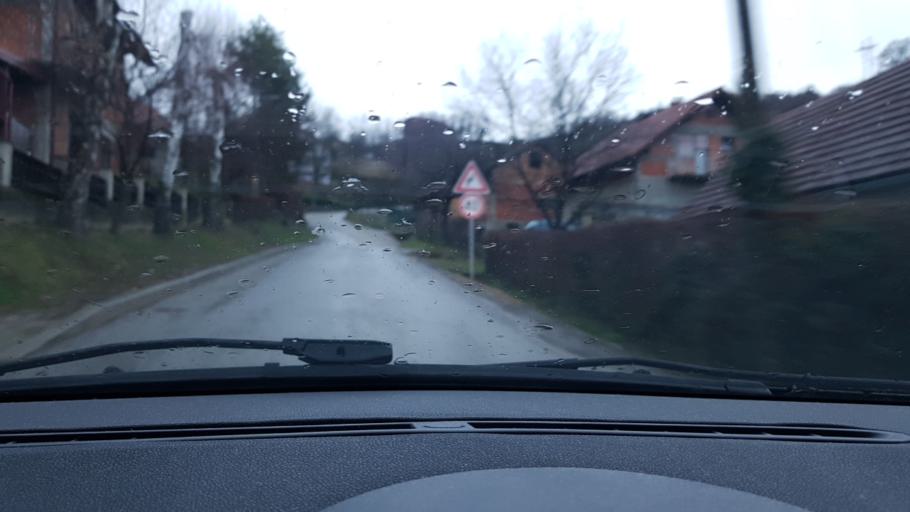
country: HR
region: Krapinsko-Zagorska
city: Bedekovcina
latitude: 45.9925
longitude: 15.9820
